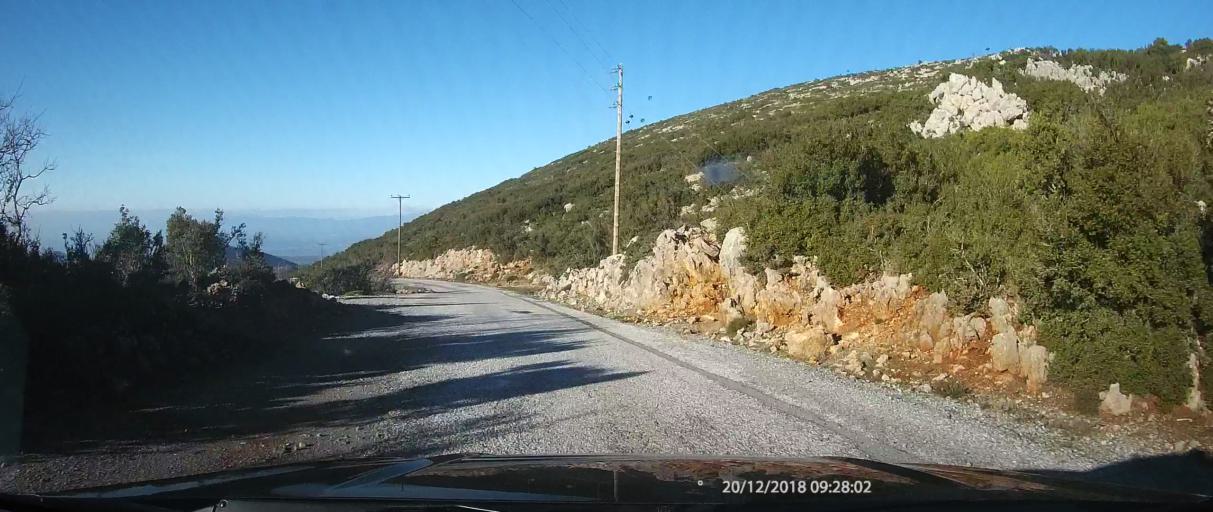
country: GR
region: Peloponnese
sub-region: Nomos Lakonias
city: Kato Glikovrisi
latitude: 36.9616
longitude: 22.8590
